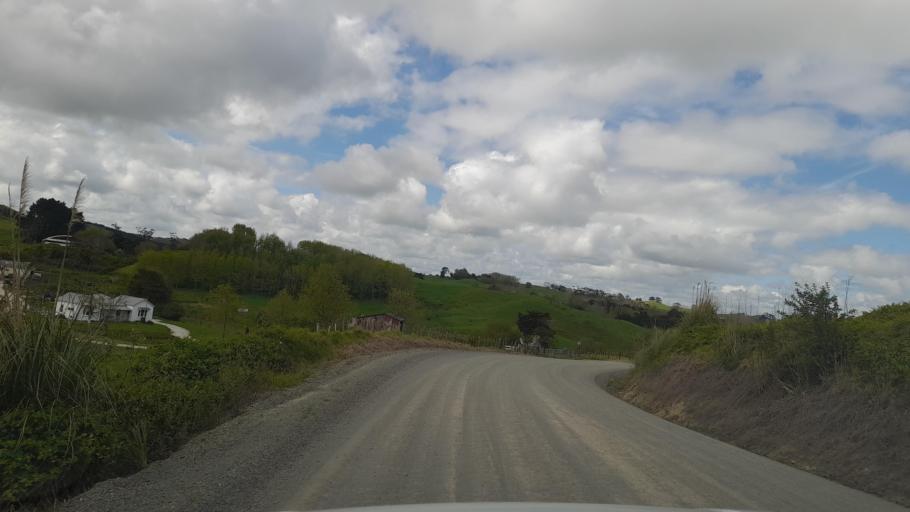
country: NZ
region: Auckland
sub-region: Auckland
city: Wellsford
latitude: -36.1560
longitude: 174.3104
